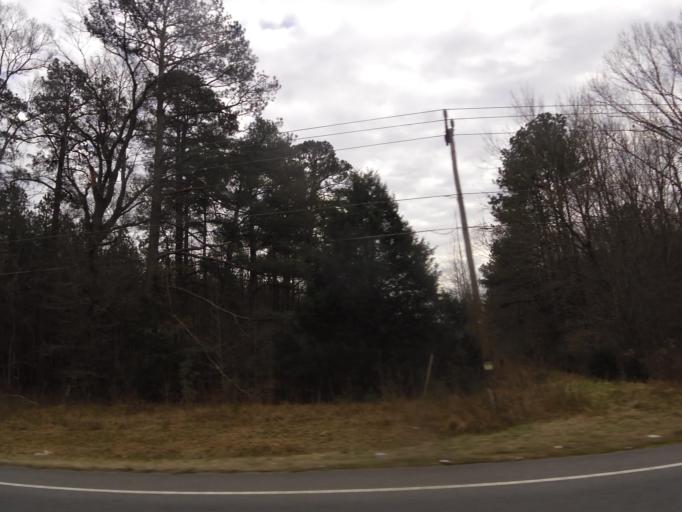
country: US
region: North Carolina
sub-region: Northampton County
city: Jackson
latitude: 36.3148
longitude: -77.2508
